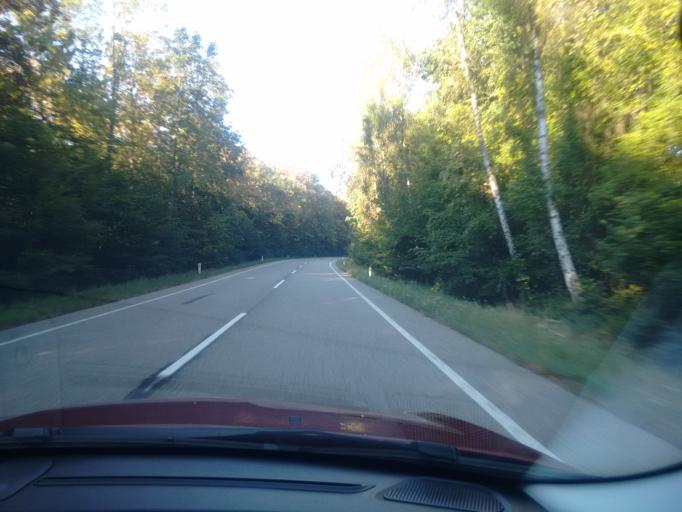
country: DE
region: Bavaria
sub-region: Upper Bavaria
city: Haiming
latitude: 48.2031
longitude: 12.9140
